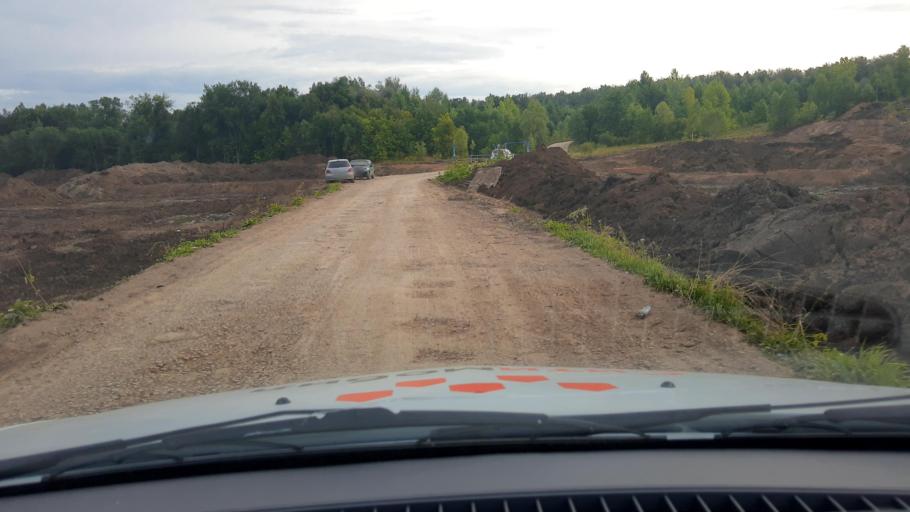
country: RU
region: Bashkortostan
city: Kabakovo
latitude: 54.7011
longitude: 56.1353
